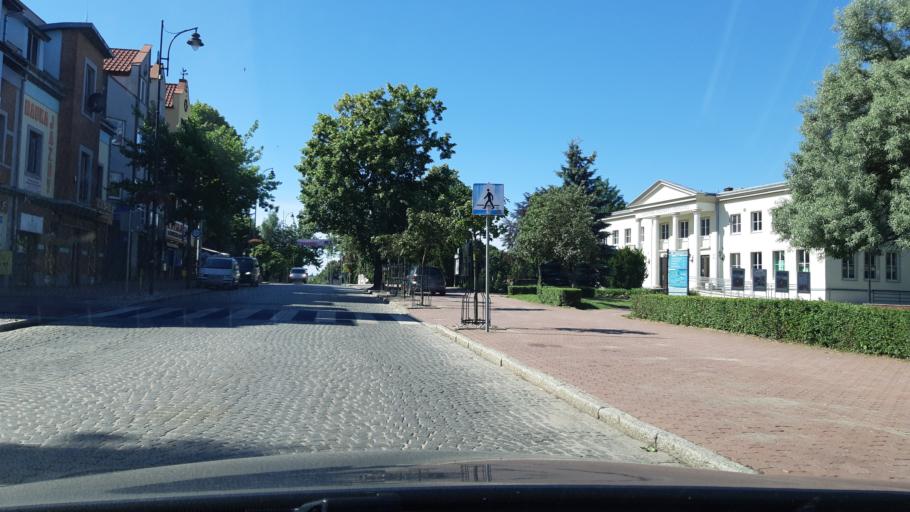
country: PL
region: Warmian-Masurian Voivodeship
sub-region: Powiat mragowski
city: Mragowo
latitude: 53.8661
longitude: 21.3055
